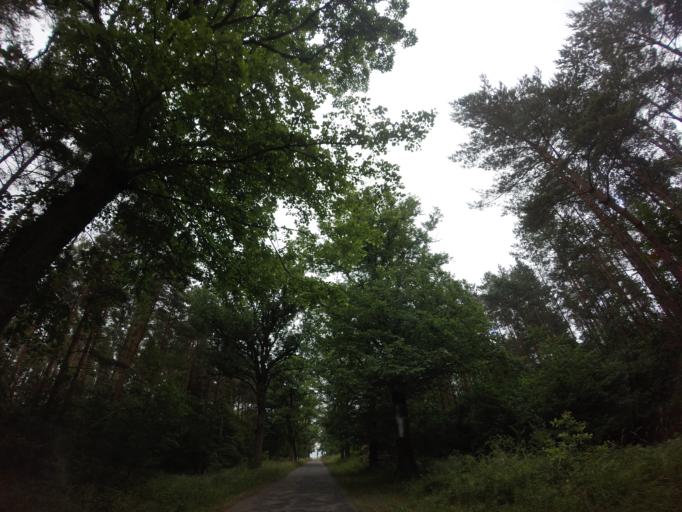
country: PL
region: West Pomeranian Voivodeship
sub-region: Powiat choszczenski
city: Krzecin
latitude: 53.0307
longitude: 15.5366
